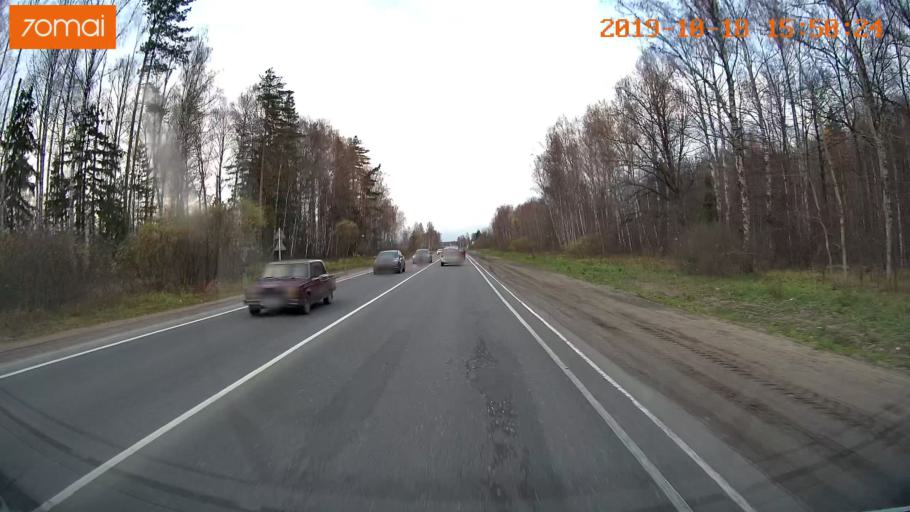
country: RU
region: Vladimir
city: Kommunar
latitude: 56.0321
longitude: 40.5605
